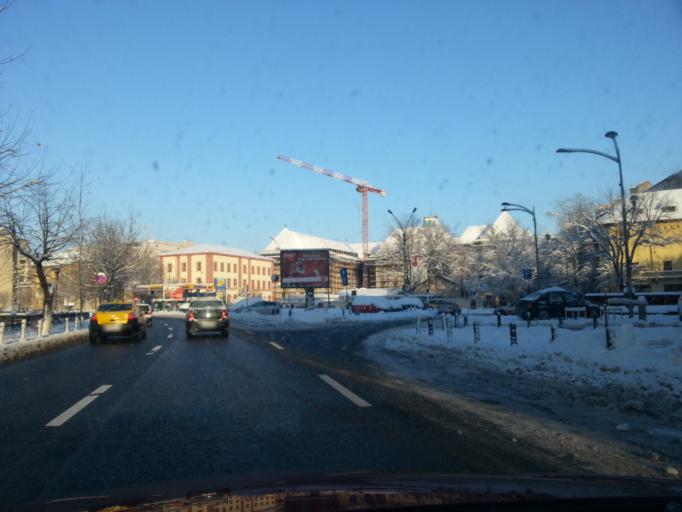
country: RO
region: Bucuresti
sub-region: Municipiul Bucuresti
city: Bucuresti
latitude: 44.4323
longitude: 26.0941
